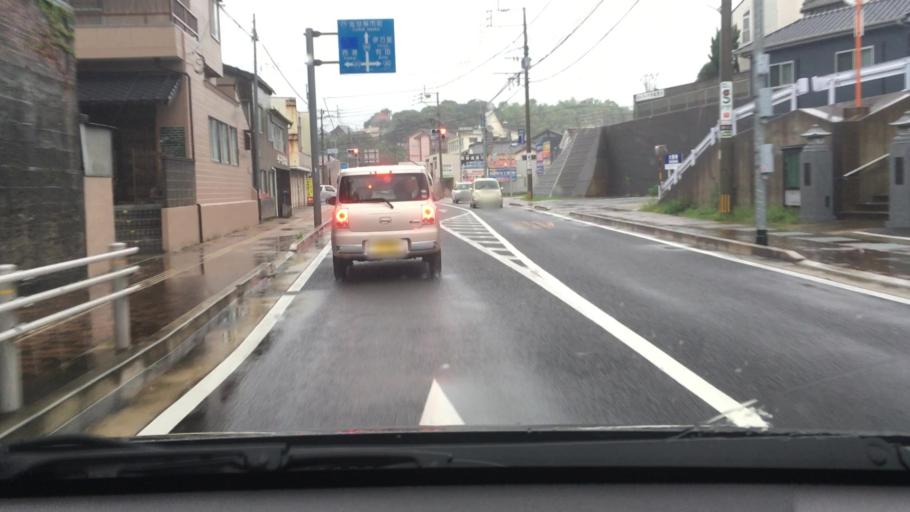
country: JP
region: Nagasaki
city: Sasebo
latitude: 33.1380
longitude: 129.7955
